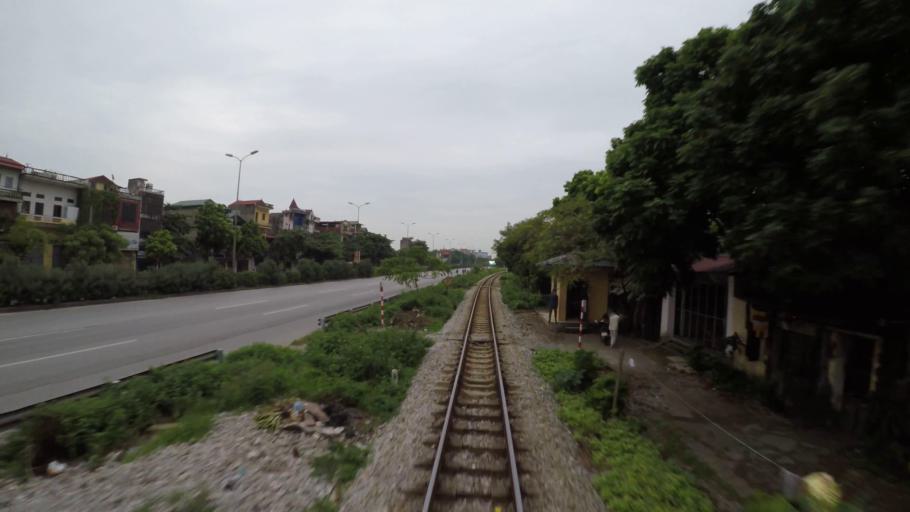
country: VN
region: Hung Yen
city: Nhu Quynh
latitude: 20.9986
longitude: 105.9692
